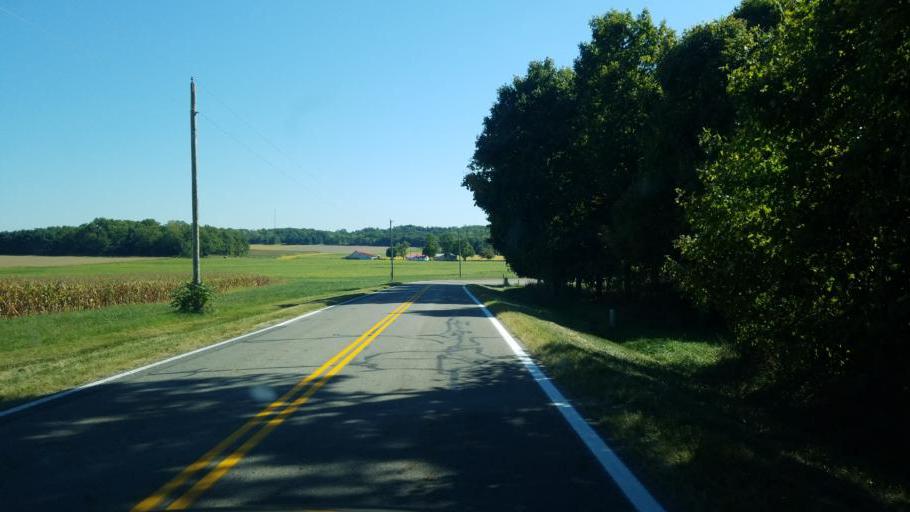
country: US
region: Ohio
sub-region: Champaign County
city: North Lewisburg
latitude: 40.2176
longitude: -83.6379
